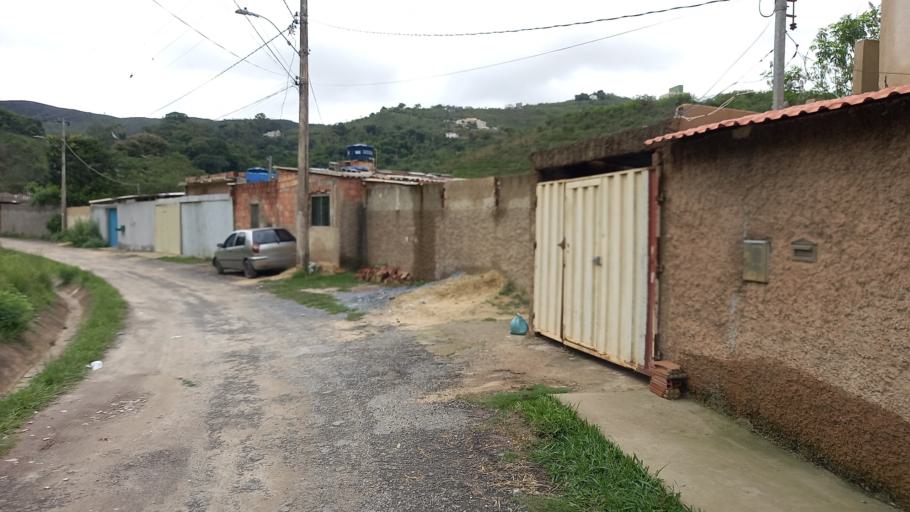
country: BR
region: Minas Gerais
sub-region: Belo Horizonte
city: Belo Horizonte
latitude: -19.9223
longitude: -43.8856
